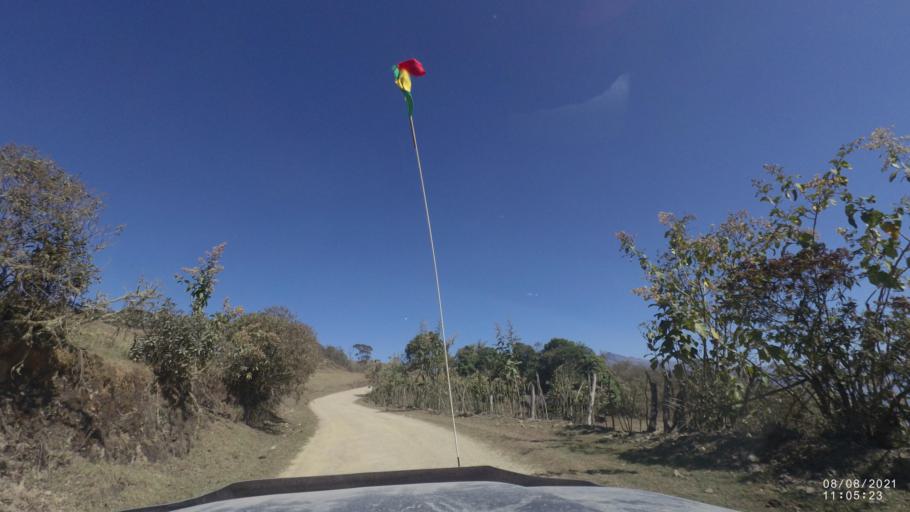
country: BO
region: Cochabamba
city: Colchani
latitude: -16.7574
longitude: -66.6820
